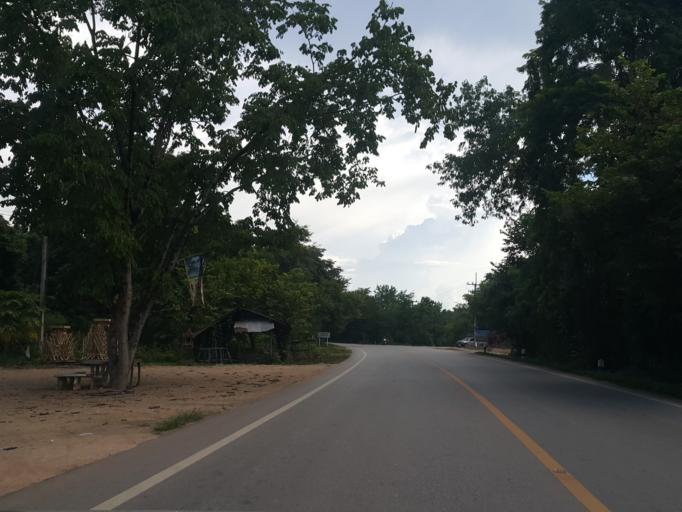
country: TH
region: Chiang Mai
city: Phrao
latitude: 19.3253
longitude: 99.1900
